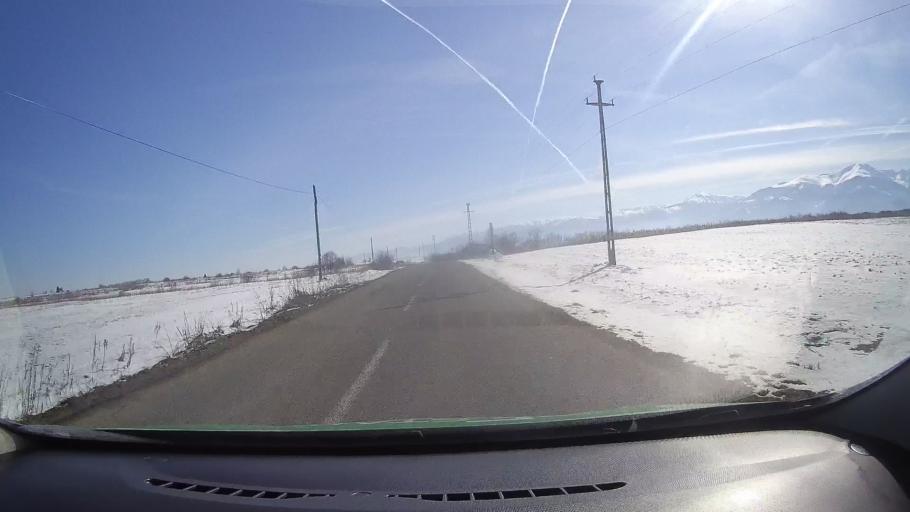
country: RO
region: Brasov
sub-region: Comuna Sambata de Sus
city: Sambata de Sus
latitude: 45.7622
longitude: 24.8034
